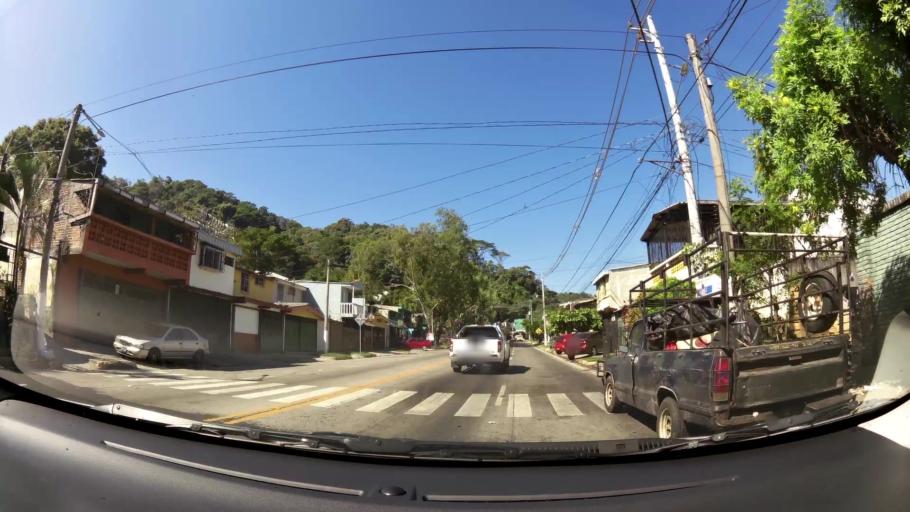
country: SV
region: La Libertad
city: Santa Tecla
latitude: 13.6668
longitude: -89.2883
